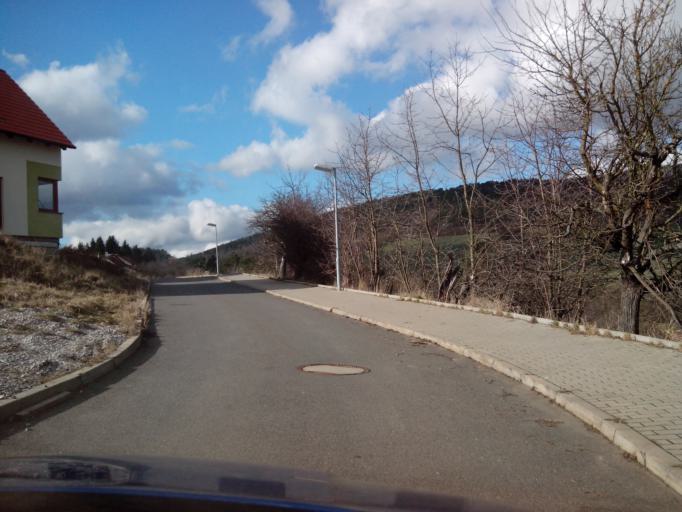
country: CZ
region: Central Bohemia
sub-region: Okres Beroun
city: Kraluv Dvur
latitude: 49.9554
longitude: 14.0398
